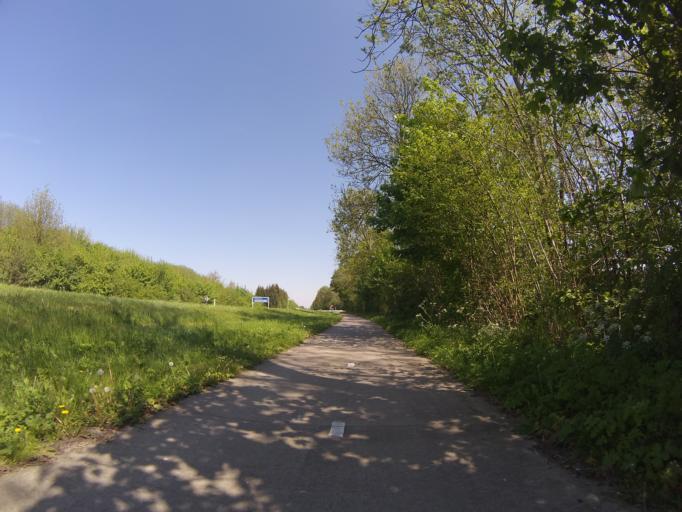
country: NL
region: Flevoland
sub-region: Gemeente Zeewolde
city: Zeewolde
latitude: 52.2916
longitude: 5.5080
